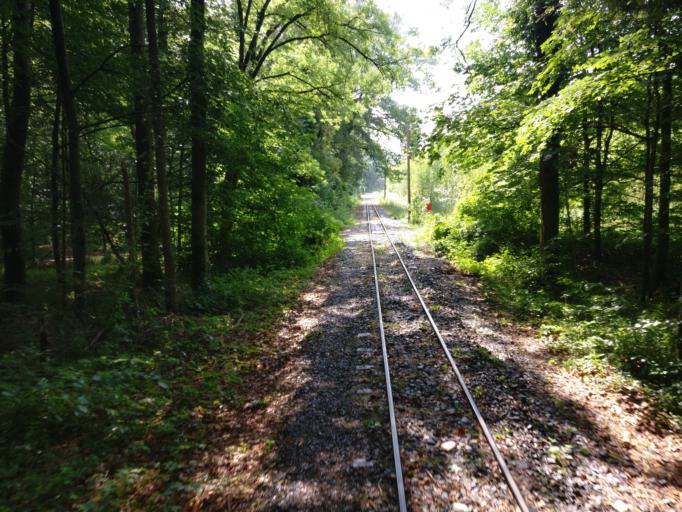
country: AT
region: Upper Austria
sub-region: Politischer Bezirk Steyr-Land
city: Garsten
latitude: 48.0482
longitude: 14.3653
